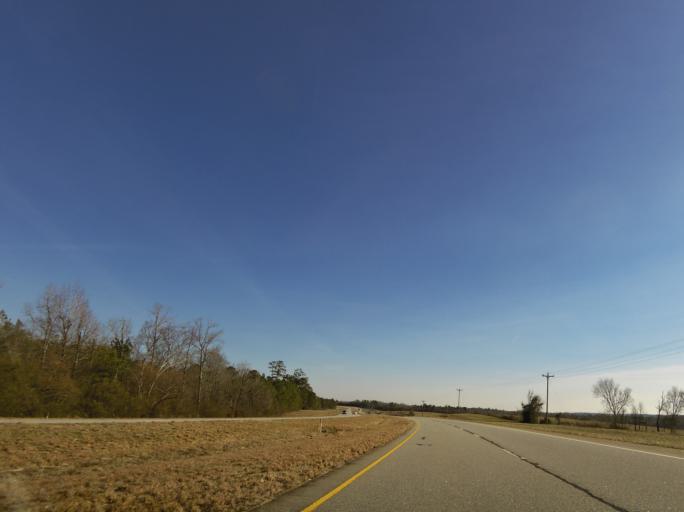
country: US
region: Georgia
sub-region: Upson County
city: Thomaston
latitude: 32.7515
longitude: -84.2420
